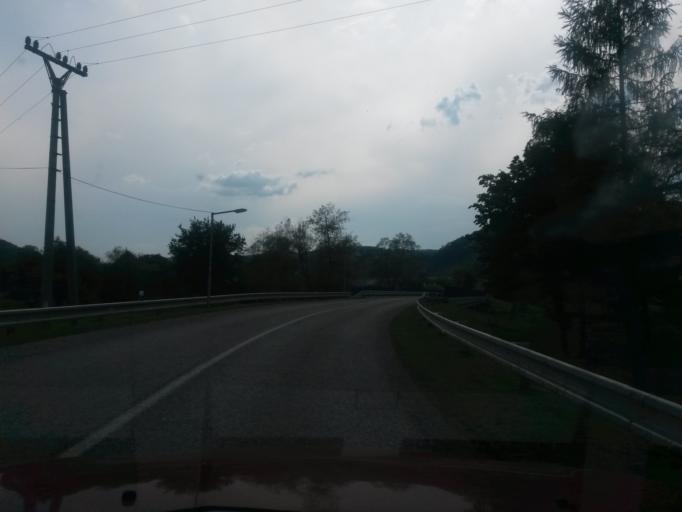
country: SK
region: Presovsky
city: Snina
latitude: 49.0452
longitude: 22.0623
